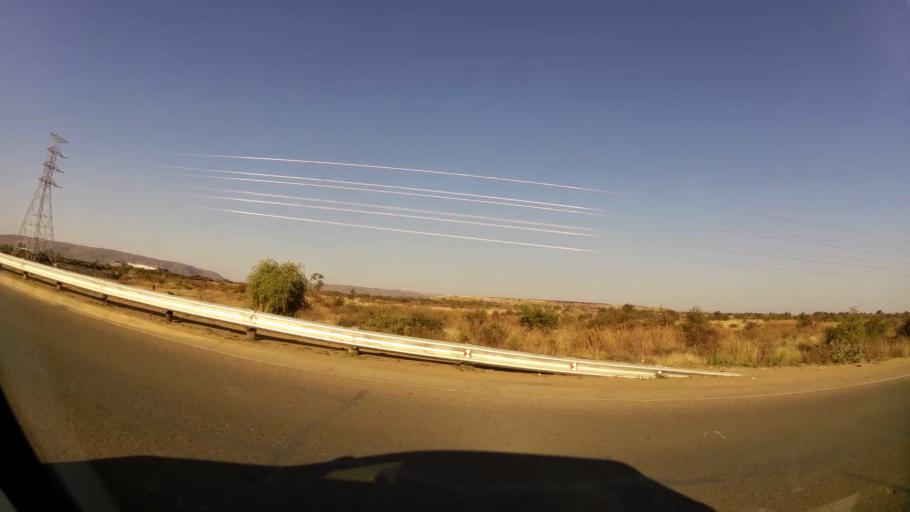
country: ZA
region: Gauteng
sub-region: City of Tshwane Metropolitan Municipality
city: Cullinan
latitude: -25.7312
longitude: 28.3992
